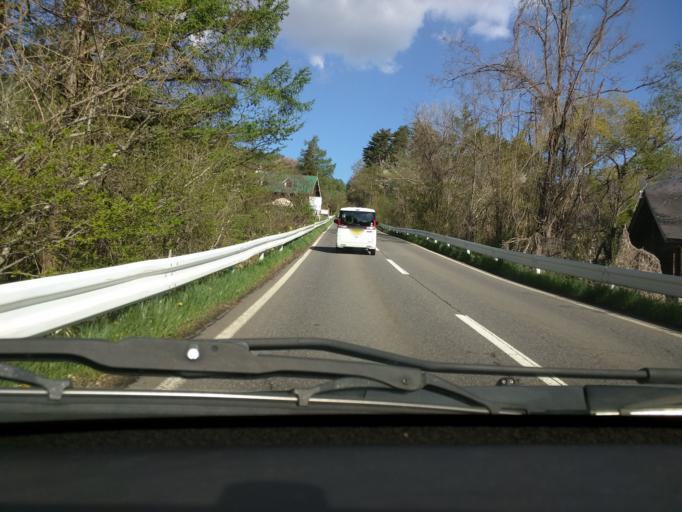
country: JP
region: Nagano
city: Nagano-shi
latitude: 36.7020
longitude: 138.1510
